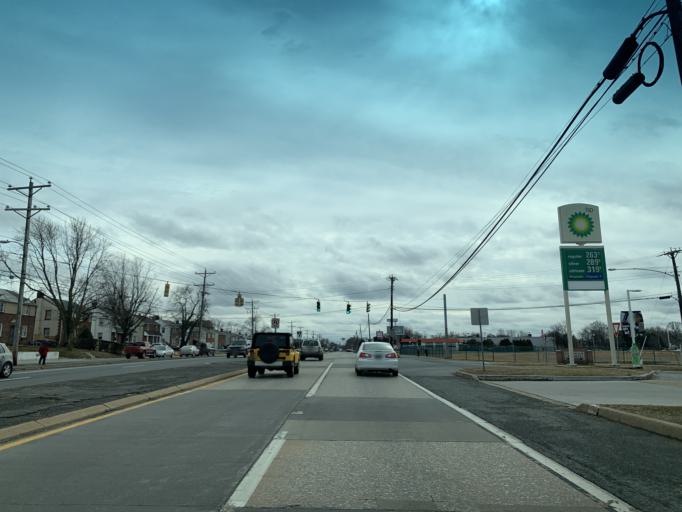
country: US
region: Delaware
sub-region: New Castle County
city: Wilmington Manor
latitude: 39.6913
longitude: -75.5553
